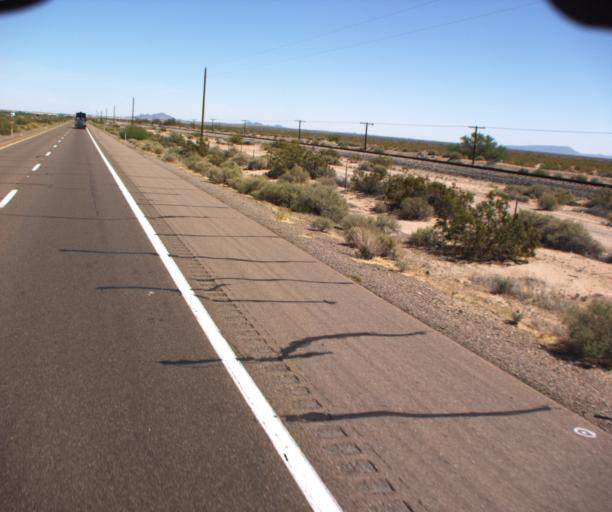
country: US
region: Arizona
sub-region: Yuma County
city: Wellton
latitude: 32.7460
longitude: -113.6734
